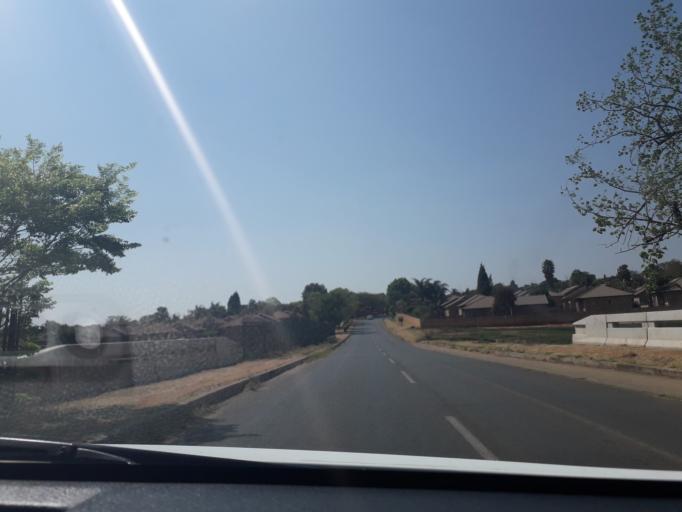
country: ZA
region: Gauteng
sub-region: City of Johannesburg Metropolitan Municipality
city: Roodepoort
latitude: -26.1252
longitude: 27.9353
